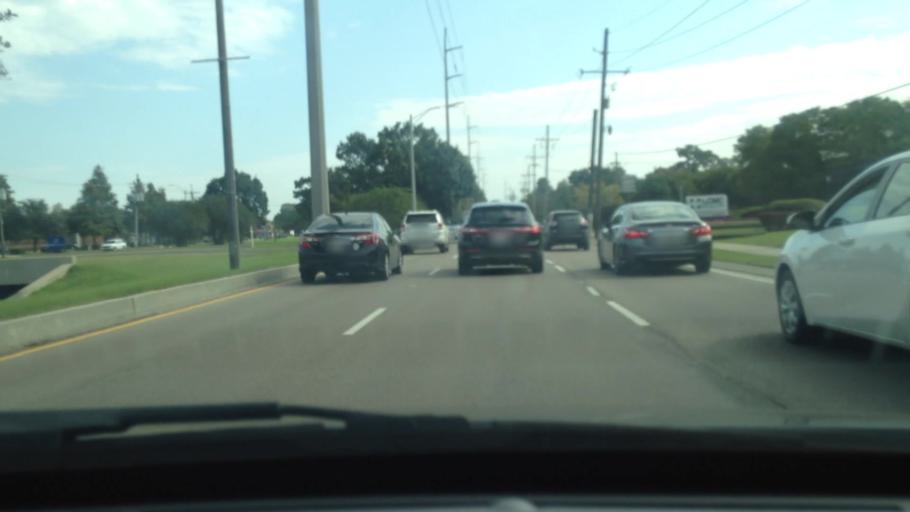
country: US
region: Louisiana
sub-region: Jefferson Parish
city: Terrytown
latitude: 29.9262
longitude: -90.0248
